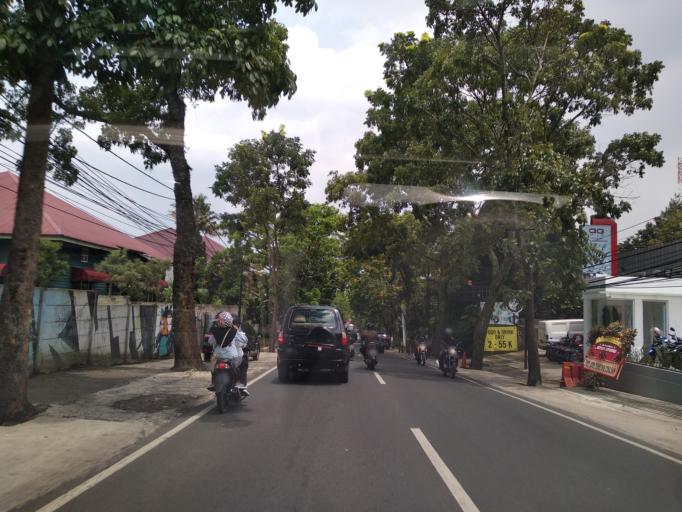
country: ID
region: West Java
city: Lembang
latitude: -6.8564
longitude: 107.5955
